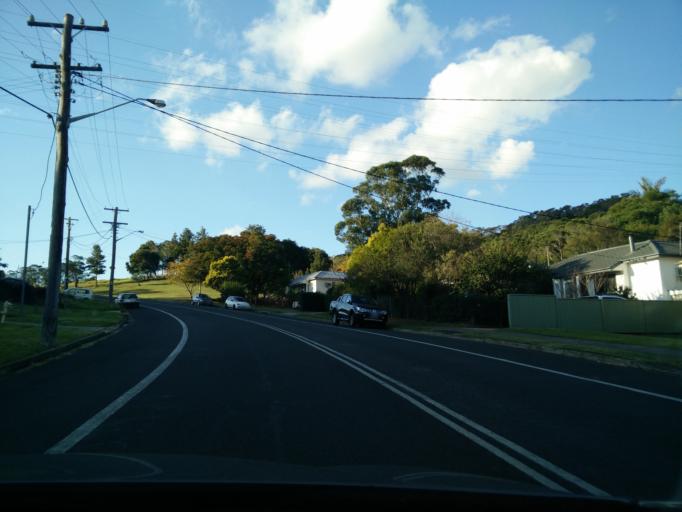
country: AU
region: New South Wales
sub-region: Wollongong
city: Berkeley
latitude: -34.4719
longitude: 150.8439
